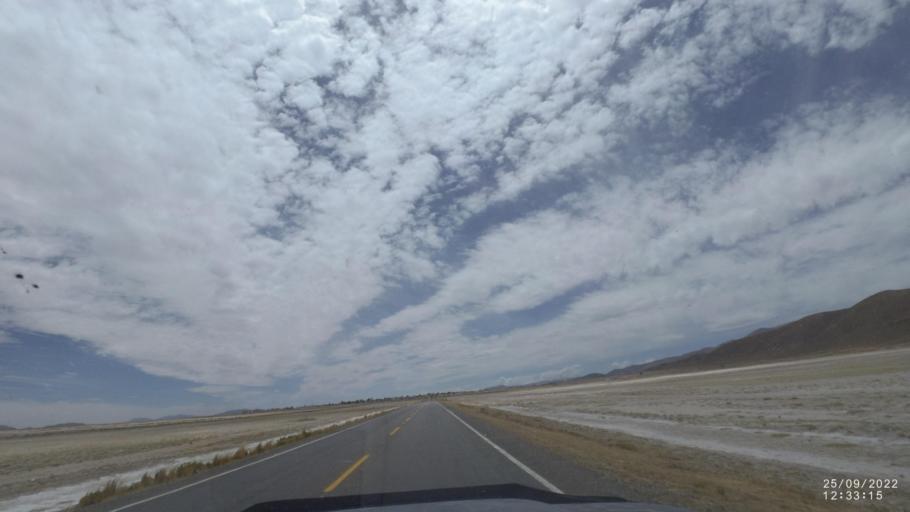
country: BO
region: Oruro
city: Machacamarca
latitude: -18.1966
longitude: -67.0128
